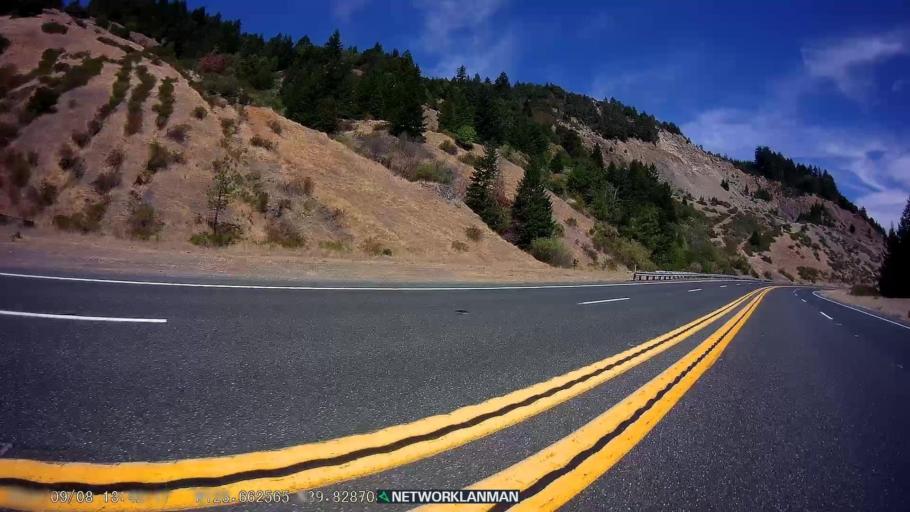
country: US
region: California
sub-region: Mendocino County
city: Laytonville
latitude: 39.8296
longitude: -123.6630
